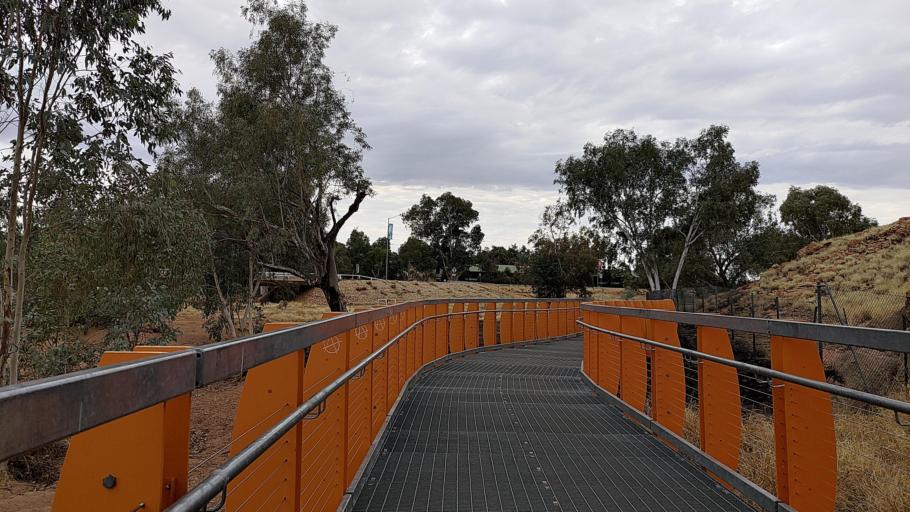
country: AU
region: Northern Territory
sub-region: Alice Springs
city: Alice Springs
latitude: -23.7039
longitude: 133.8839
